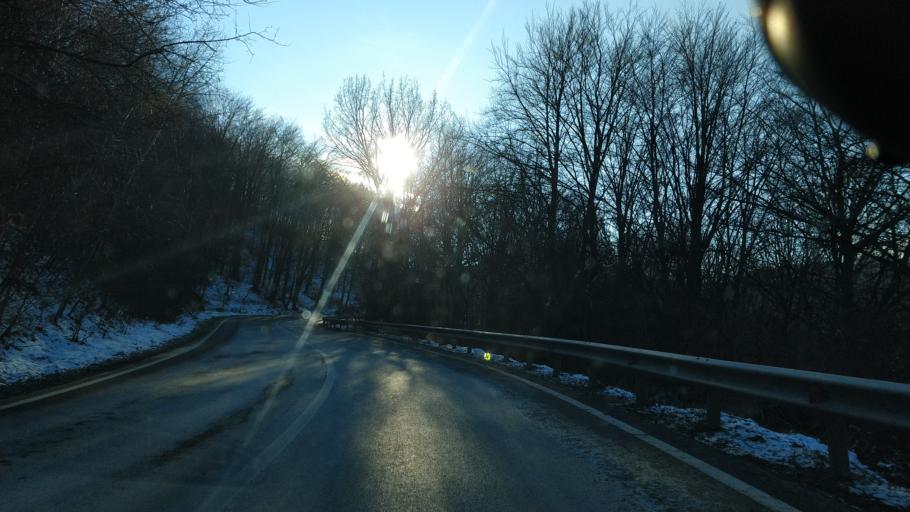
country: RO
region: Bacau
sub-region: Comuna Luizi-Calugara
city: Luizi-Calugara
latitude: 46.5513
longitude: 26.8205
